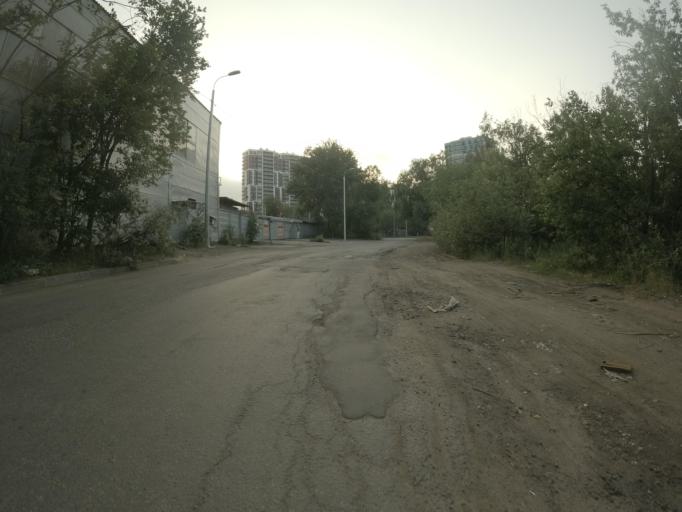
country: RU
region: St.-Petersburg
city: Krasnogvargeisky
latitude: 59.9548
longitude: 30.4517
